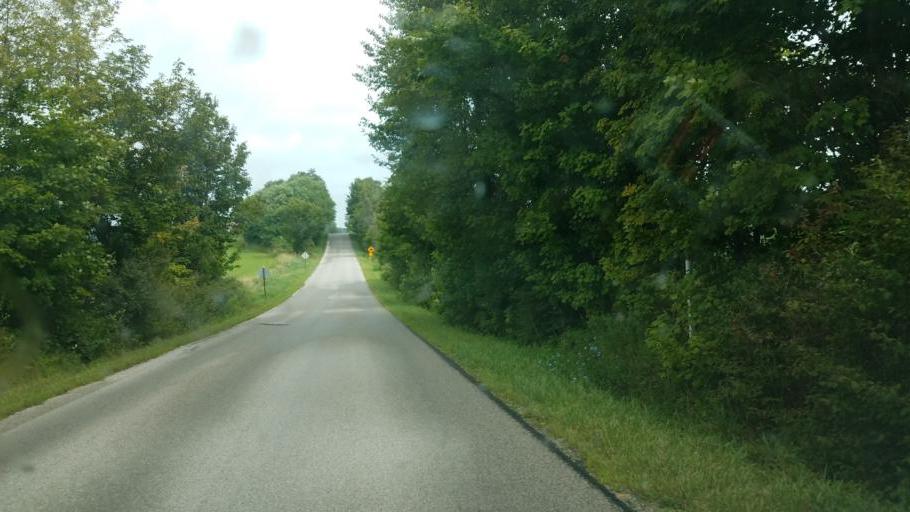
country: US
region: Ohio
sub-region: Morrow County
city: Cardington
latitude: 40.4296
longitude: -82.8089
